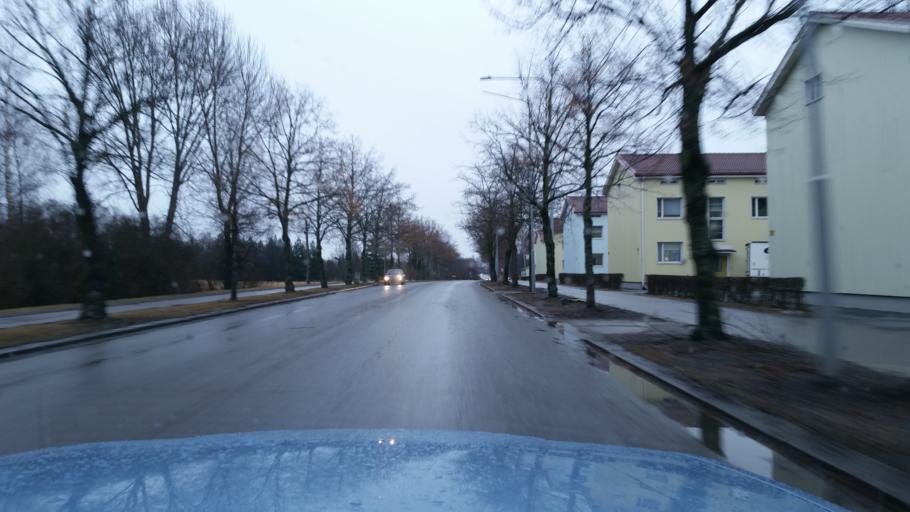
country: FI
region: Pirkanmaa
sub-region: Tampere
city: Tampere
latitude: 61.4843
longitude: 23.7993
